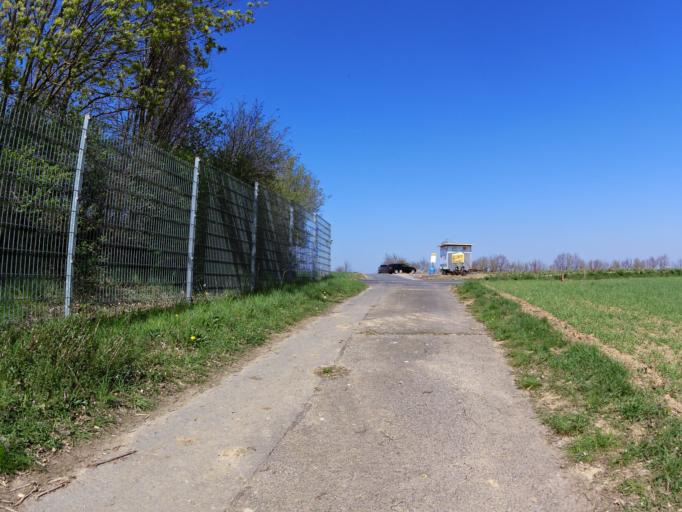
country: DE
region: Bavaria
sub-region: Regierungsbezirk Unterfranken
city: Biebelried
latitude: 49.7834
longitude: 10.0701
